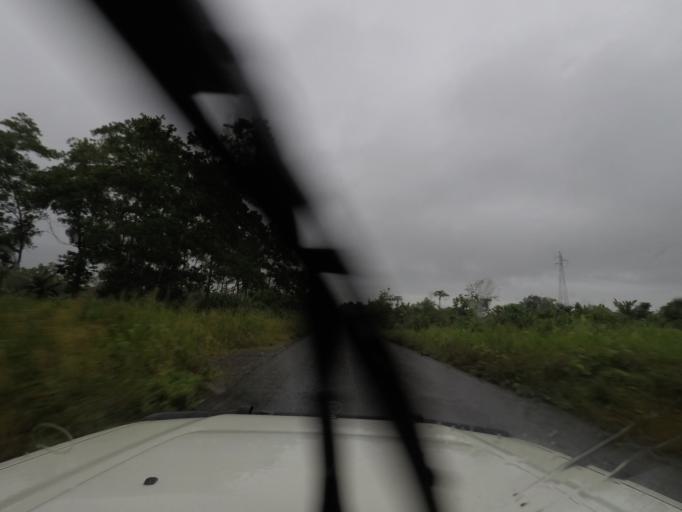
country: PG
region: Madang
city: Madang
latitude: -5.3524
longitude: 145.7101
